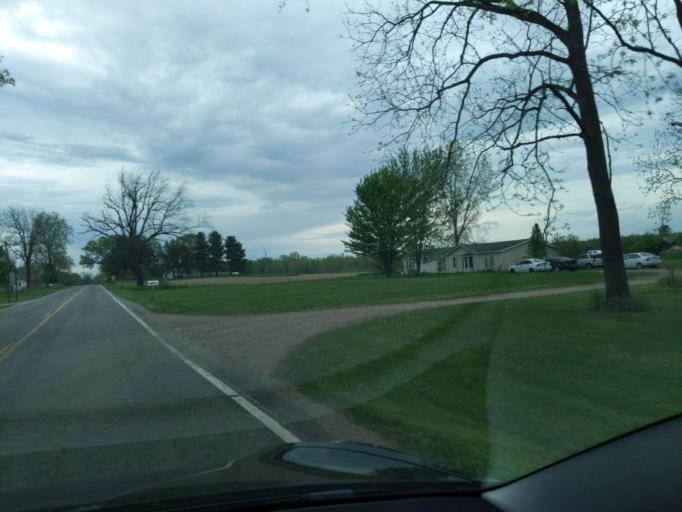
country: US
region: Michigan
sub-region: Ingham County
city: Stockbridge
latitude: 42.4511
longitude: -84.2584
